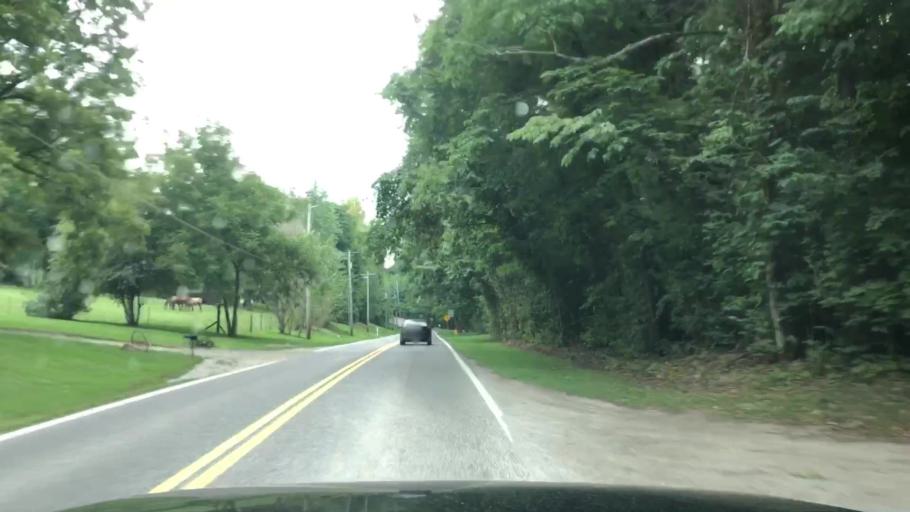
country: US
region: Missouri
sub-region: Saint Louis County
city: Hazelwood
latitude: 38.8102
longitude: -90.3857
